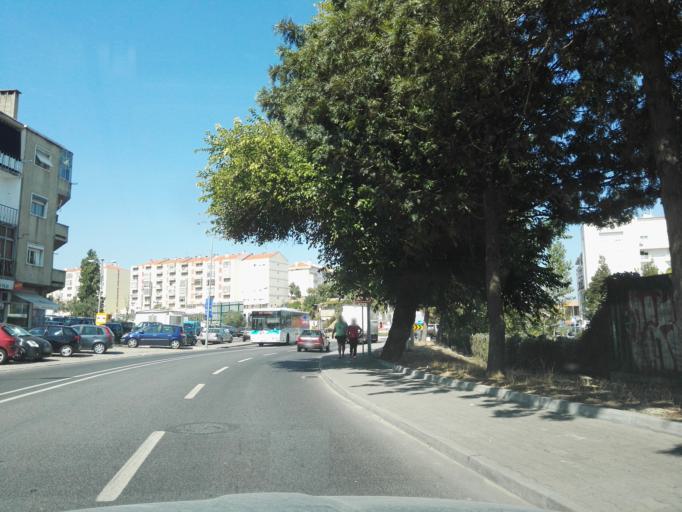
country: PT
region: Lisbon
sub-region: Vila Franca de Xira
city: Povoa de Santa Iria
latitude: 38.8655
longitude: -9.0604
